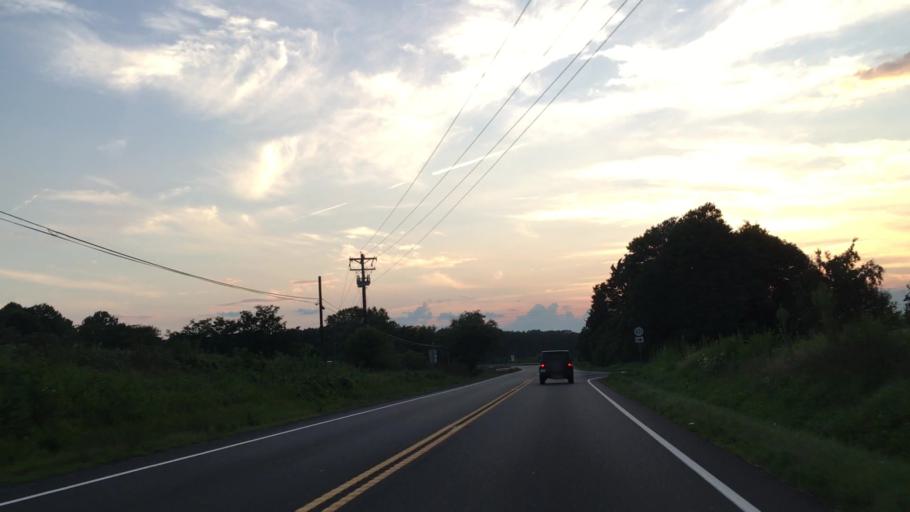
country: US
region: Virginia
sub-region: Orange County
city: Orange
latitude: 38.2717
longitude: -77.9021
